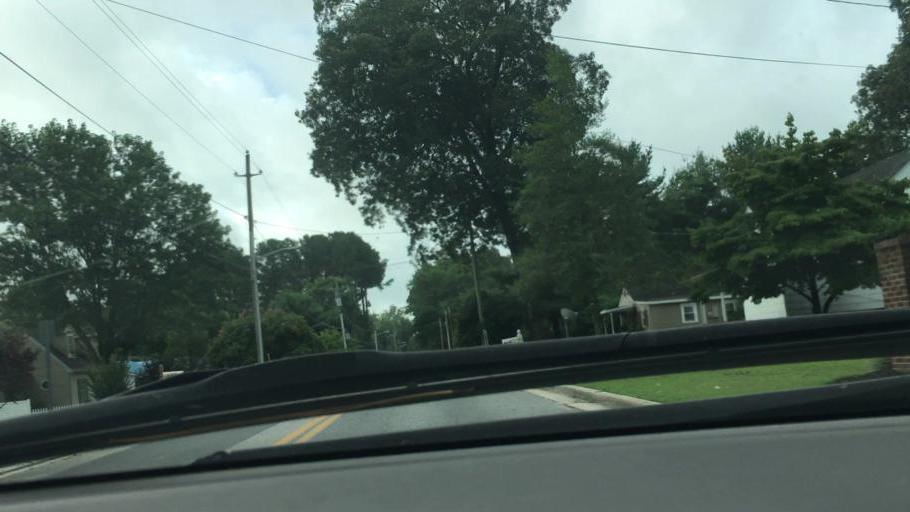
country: US
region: Maryland
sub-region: Wicomico County
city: Fruitland
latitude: 38.3335
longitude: -75.6276
